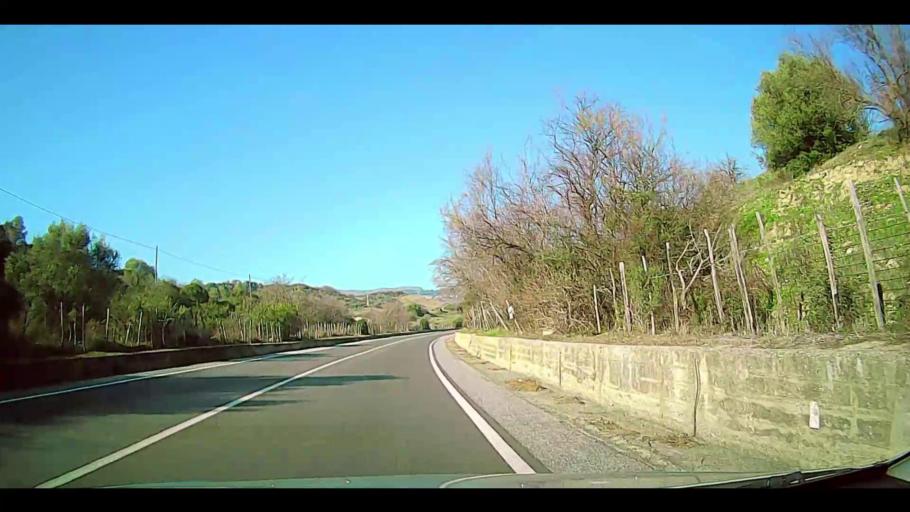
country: IT
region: Calabria
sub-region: Provincia di Crotone
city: Cotronei
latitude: 39.1859
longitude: 16.8214
